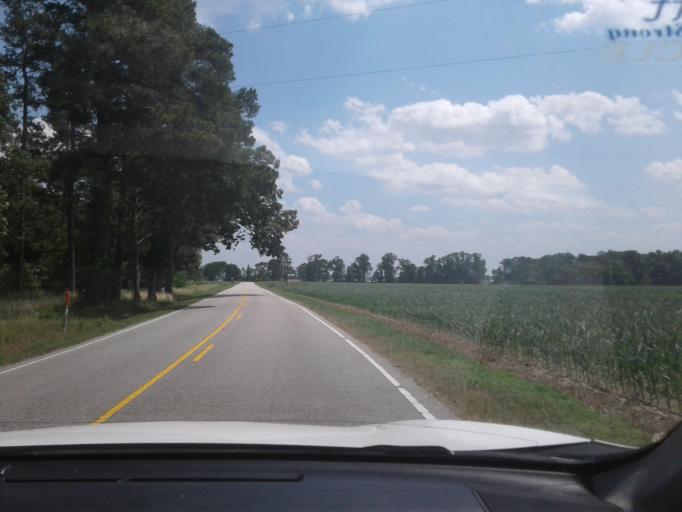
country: US
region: North Carolina
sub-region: Harnett County
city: Erwin
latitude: 35.2725
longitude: -78.6720
